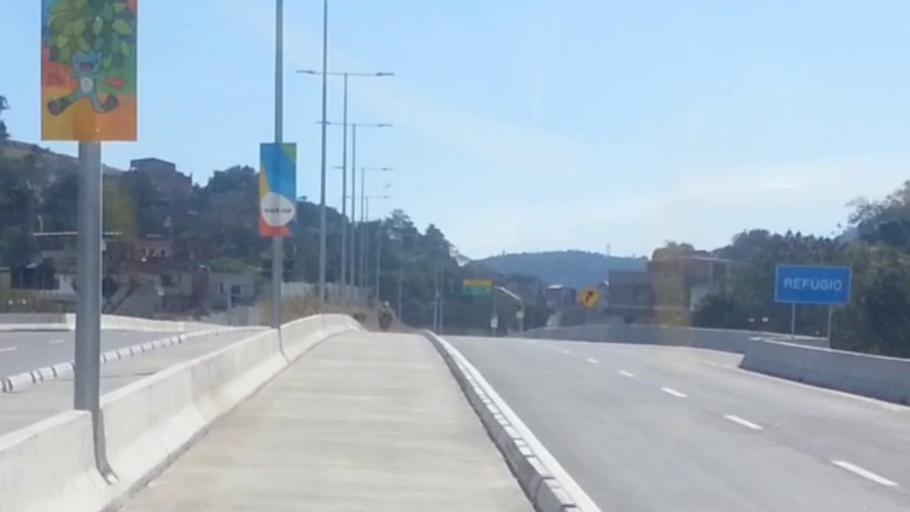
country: BR
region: Rio de Janeiro
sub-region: Nilopolis
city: Nilopolis
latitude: -22.9266
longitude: -43.3966
